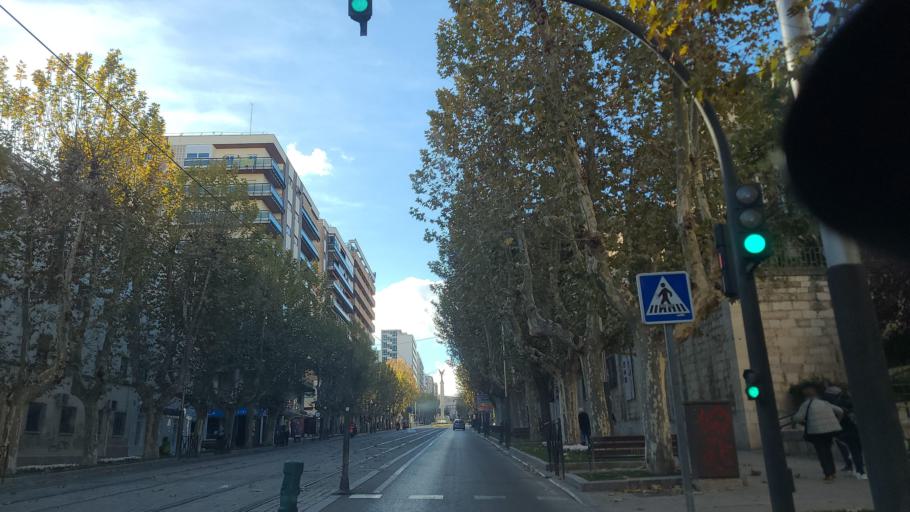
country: ES
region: Andalusia
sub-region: Provincia de Jaen
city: Jaen
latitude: 37.7748
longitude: -3.7891
